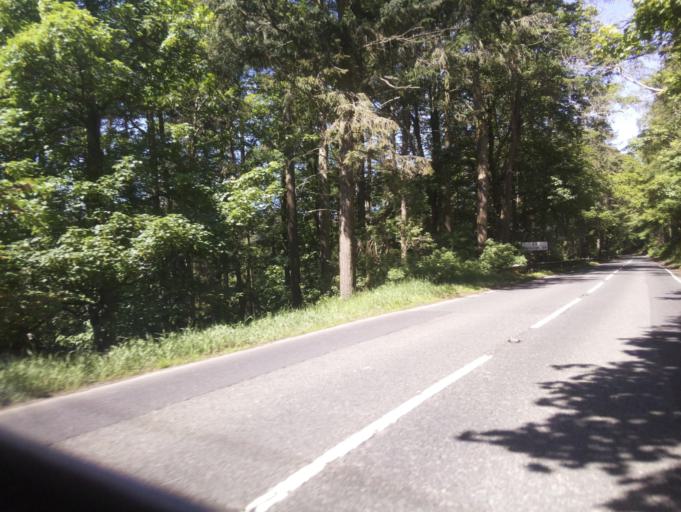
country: GB
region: Scotland
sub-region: The Scottish Borders
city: Galashiels
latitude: 55.6497
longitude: -2.8602
